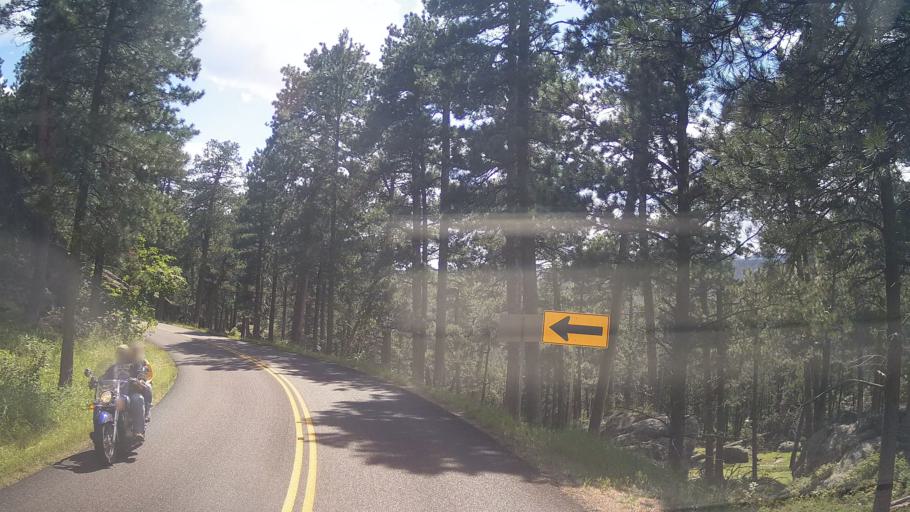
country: US
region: South Dakota
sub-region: Custer County
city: Custer
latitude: 43.8630
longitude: -103.4414
